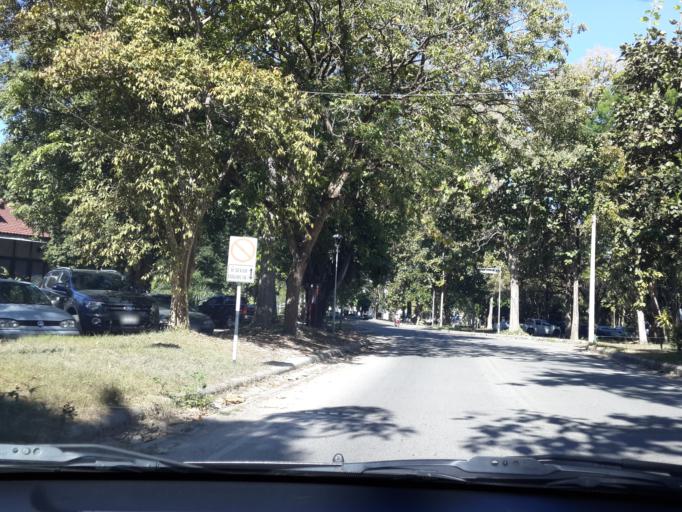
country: TH
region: Chiang Mai
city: Chiang Mai
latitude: 18.7998
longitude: 98.9556
